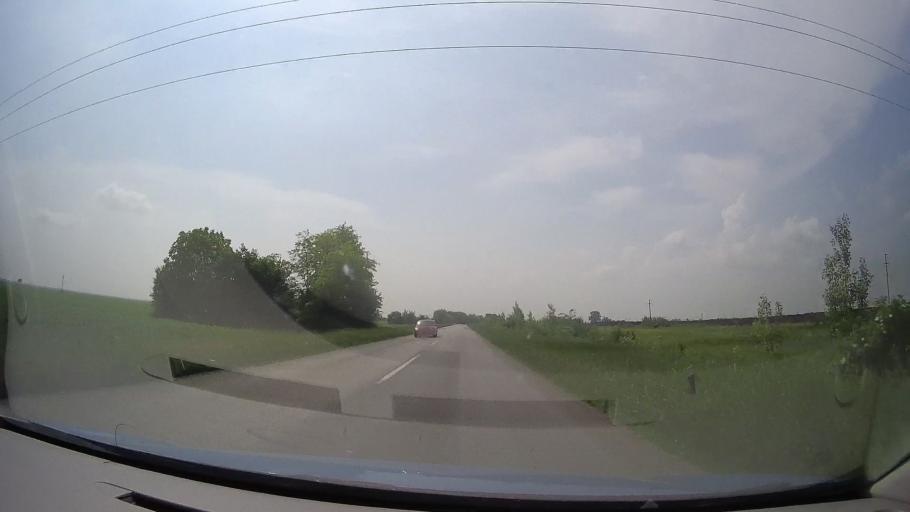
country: RS
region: Autonomna Pokrajina Vojvodina
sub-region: Juznobanatski Okrug
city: Kovacica
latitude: 45.0847
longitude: 20.6387
